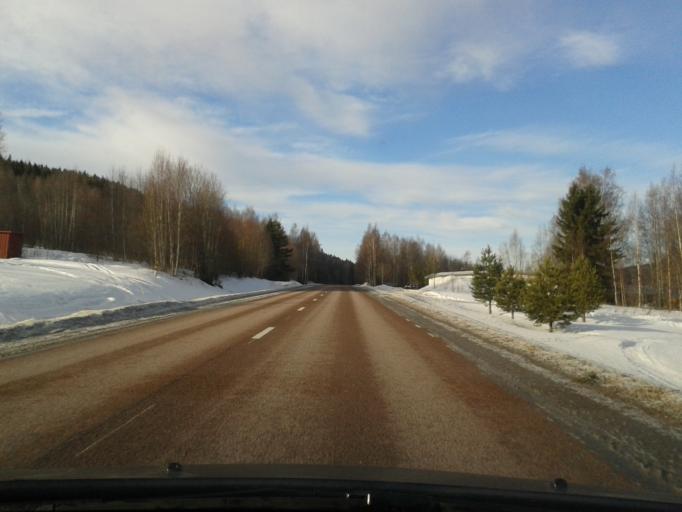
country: SE
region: Vaesternorrland
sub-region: OErnskoeldsviks Kommun
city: Bjasta
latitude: 63.3395
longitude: 18.5087
